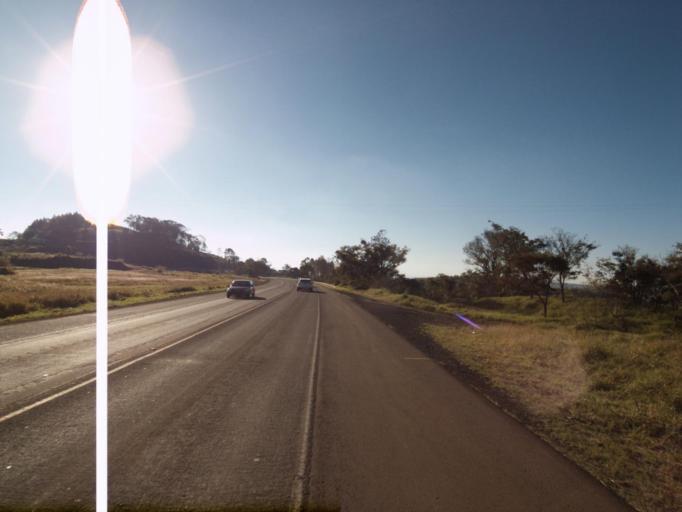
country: BR
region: Santa Catarina
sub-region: Chapeco
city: Chapeco
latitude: -26.9814
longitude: -52.7350
